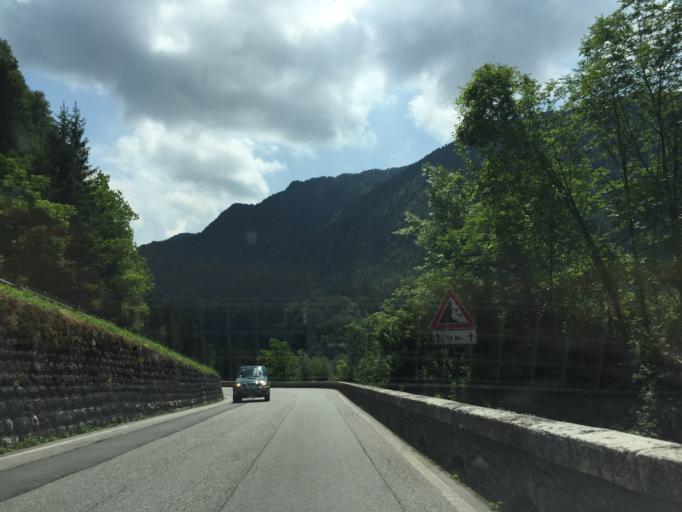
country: IT
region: Veneto
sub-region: Provincia di Belluno
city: Lamon
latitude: 46.0294
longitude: 11.7637
